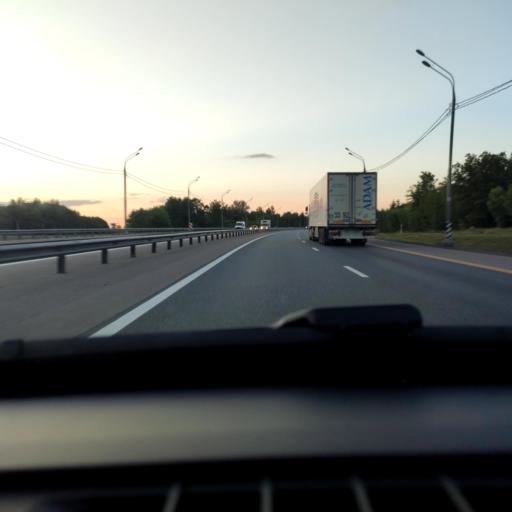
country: RU
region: Lipetsk
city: Khlevnoye
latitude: 52.2466
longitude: 39.0658
